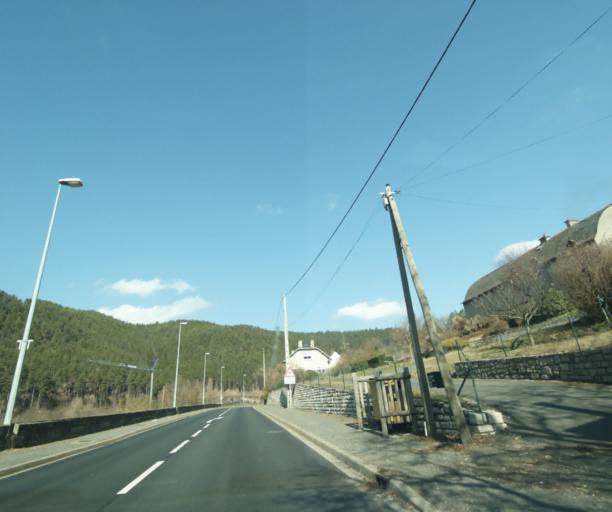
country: FR
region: Languedoc-Roussillon
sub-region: Departement de la Lozere
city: Mende
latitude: 44.5241
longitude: 3.5107
